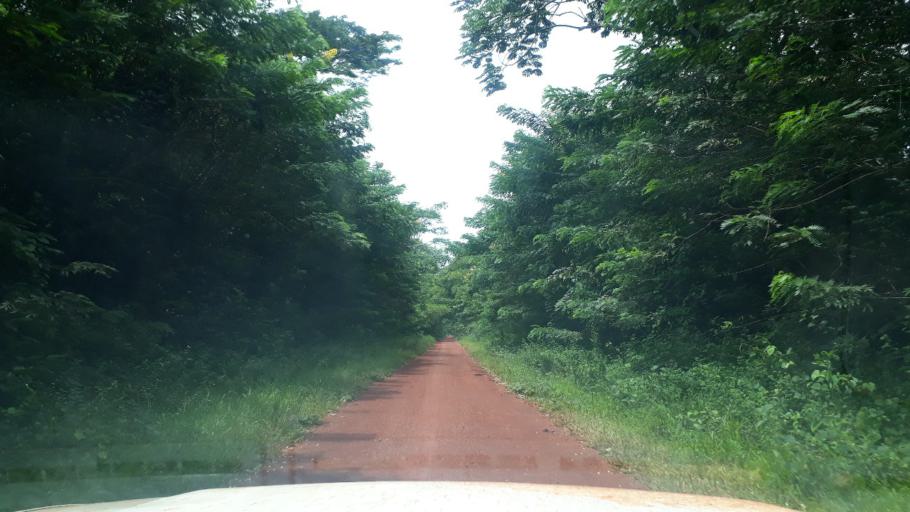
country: CD
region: Eastern Province
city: Aketi
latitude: 2.9312
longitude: 24.0909
